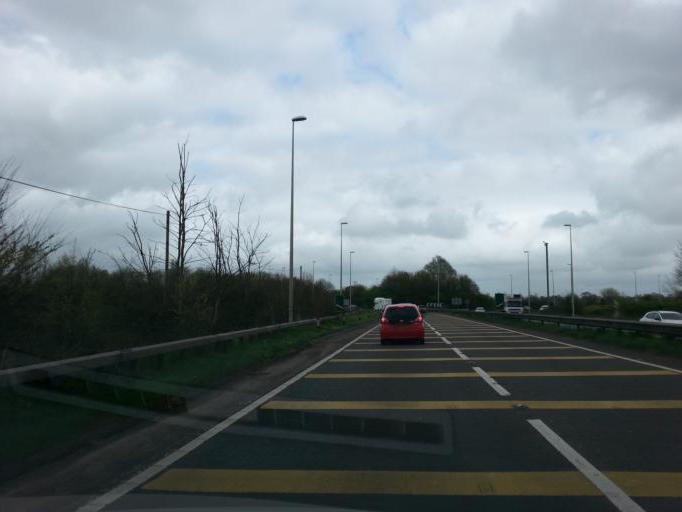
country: GB
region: England
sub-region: Somerset
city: Stoke-sub-Hamdon
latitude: 50.9667
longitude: -2.7434
